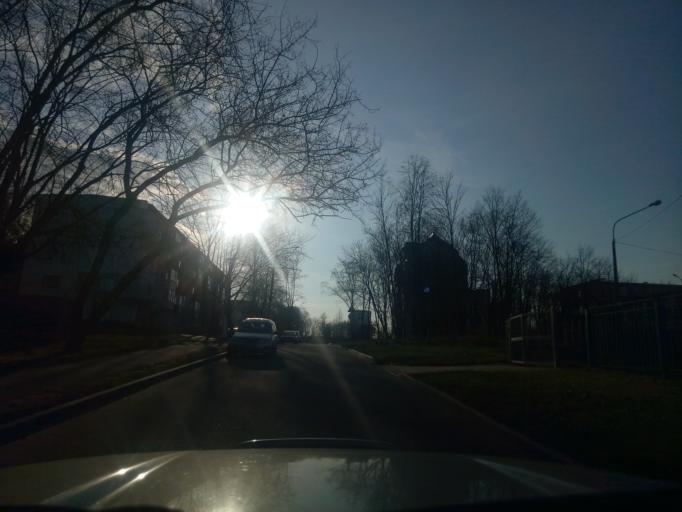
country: BY
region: Minsk
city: Novoye Medvezhino
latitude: 53.9149
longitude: 27.5005
